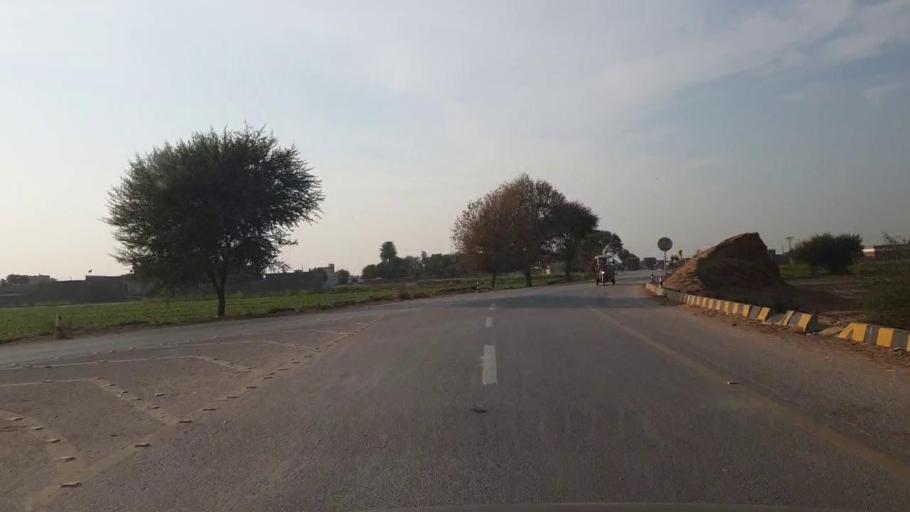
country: PK
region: Sindh
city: Shahpur Chakar
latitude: 26.1638
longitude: 68.6293
